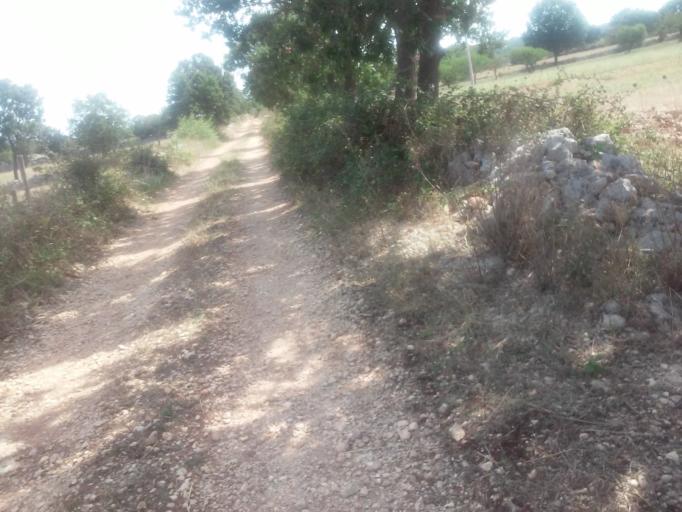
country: IT
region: Apulia
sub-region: Provincia di Bari
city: Gioia del Colle
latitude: 40.8199
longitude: 16.9607
